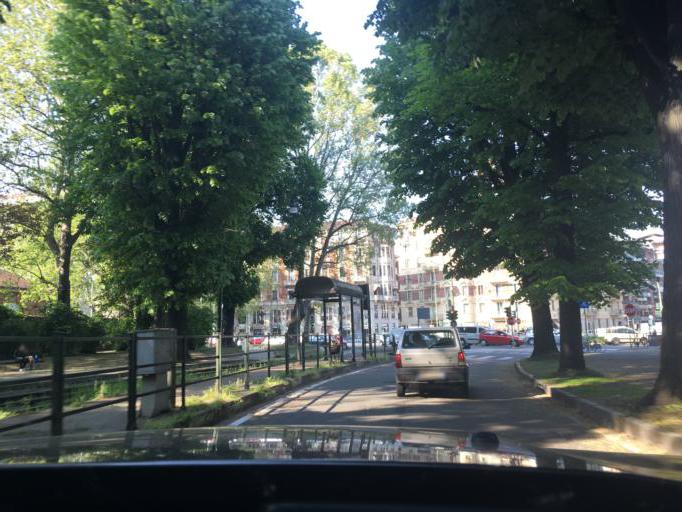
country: IT
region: Piedmont
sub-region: Provincia di Torino
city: Turin
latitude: 45.0740
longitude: 7.6891
